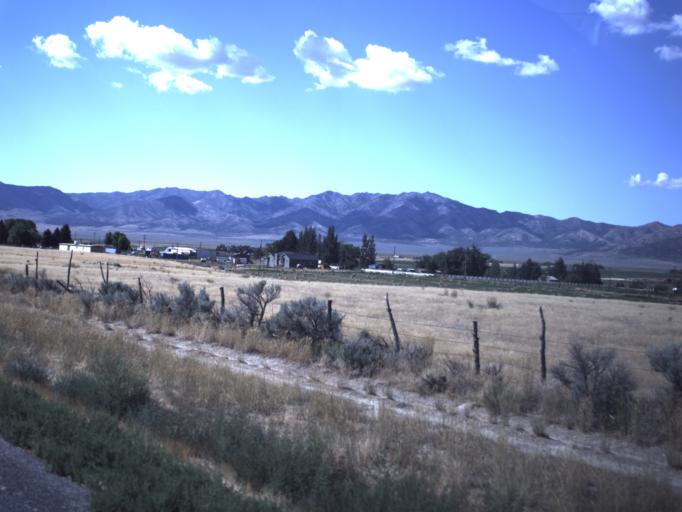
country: US
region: Utah
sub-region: Tooele County
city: Tooele
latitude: 40.0904
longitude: -112.4309
